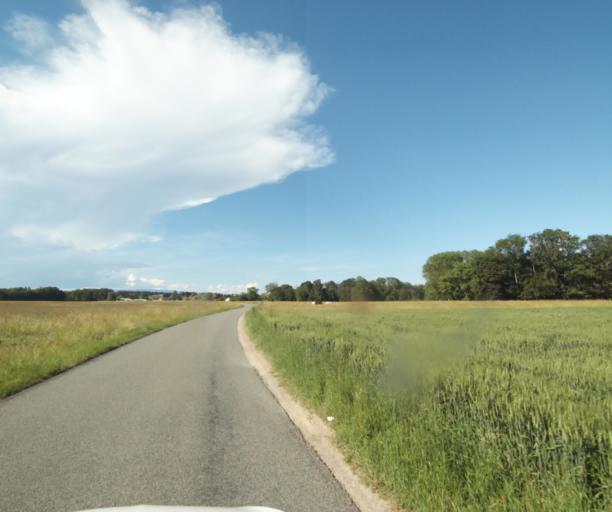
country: FR
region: Rhone-Alpes
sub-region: Departement de la Haute-Savoie
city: Massongy
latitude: 46.3401
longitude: 6.3280
